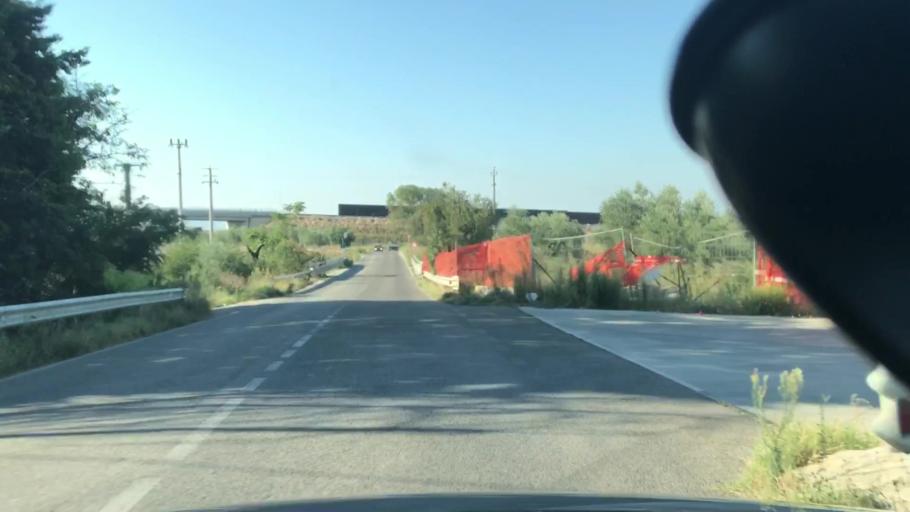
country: IT
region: Basilicate
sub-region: Provincia di Matera
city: La Martella
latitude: 40.6595
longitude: 16.5618
